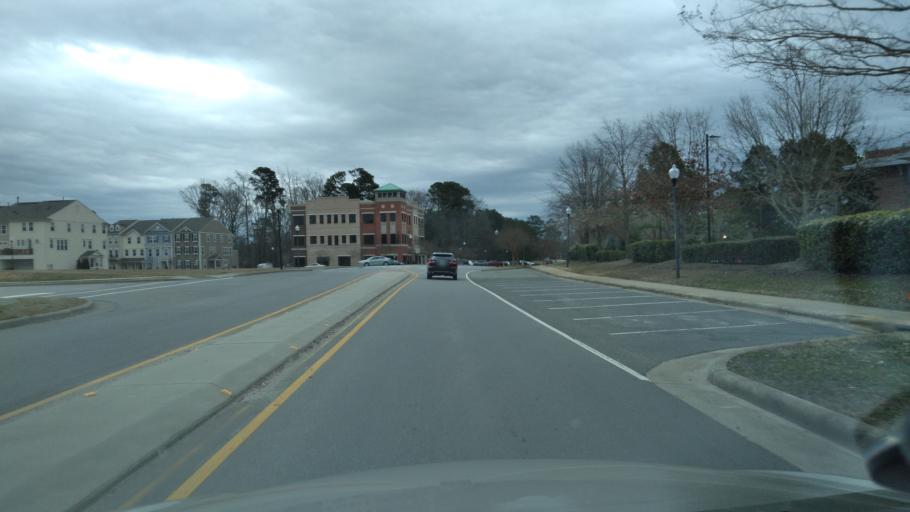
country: US
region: North Carolina
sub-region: Wake County
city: Apex
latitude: 35.7354
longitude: -78.8475
